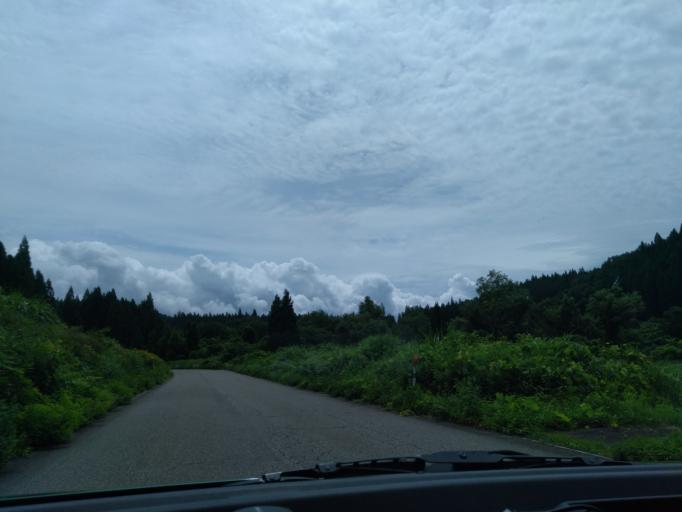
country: JP
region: Akita
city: Kakunodatemachi
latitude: 39.5720
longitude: 140.6332
